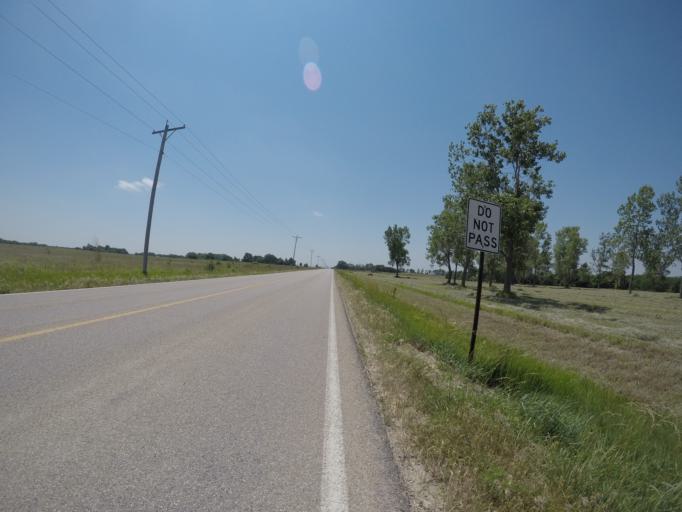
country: US
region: Kansas
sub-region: Riley County
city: Manhattan
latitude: 39.2242
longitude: -96.4407
